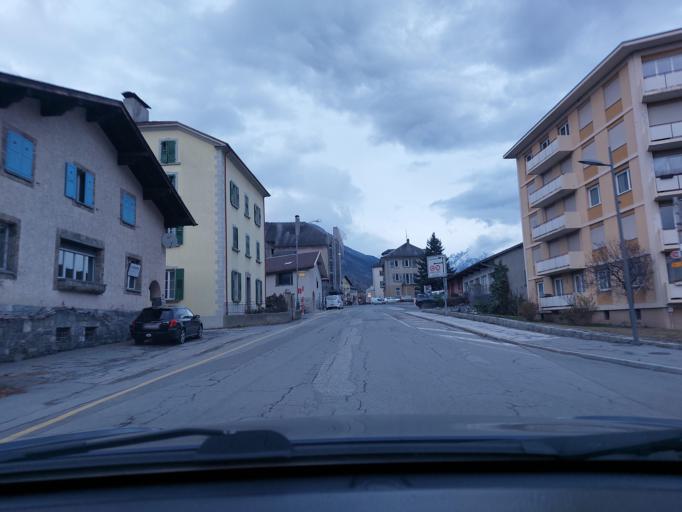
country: CH
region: Valais
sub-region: Conthey District
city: Chamoson
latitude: 46.1909
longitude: 7.2364
